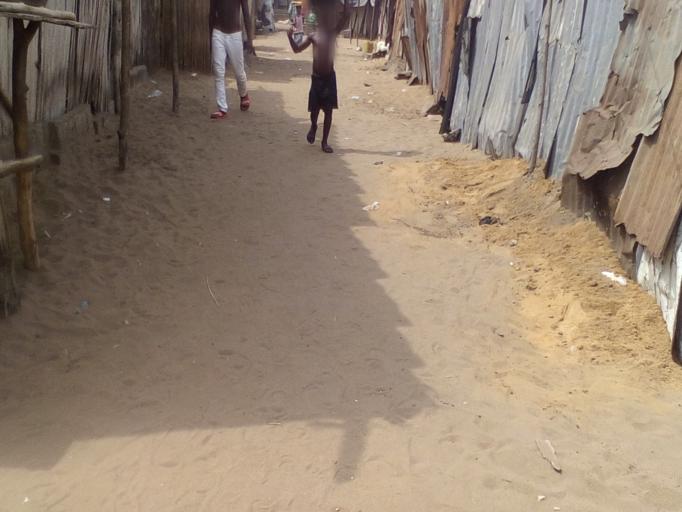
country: BJ
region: Littoral
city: Cotonou
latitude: 6.3560
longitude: 2.4528
